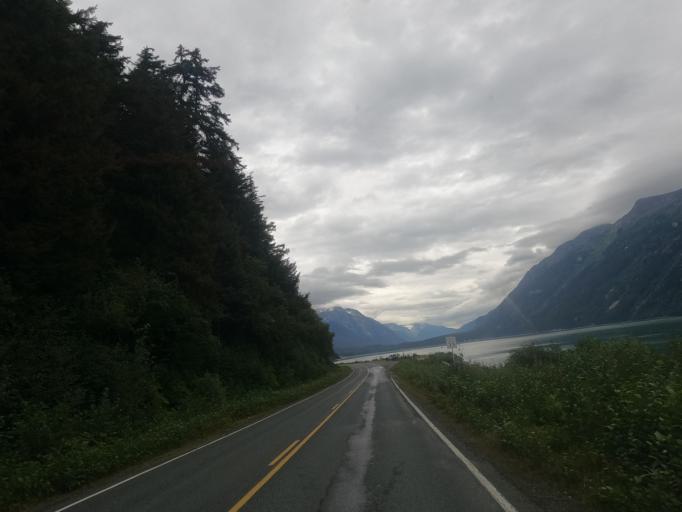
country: US
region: Alaska
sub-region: Haines Borough
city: Haines
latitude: 59.2901
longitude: -135.4925
